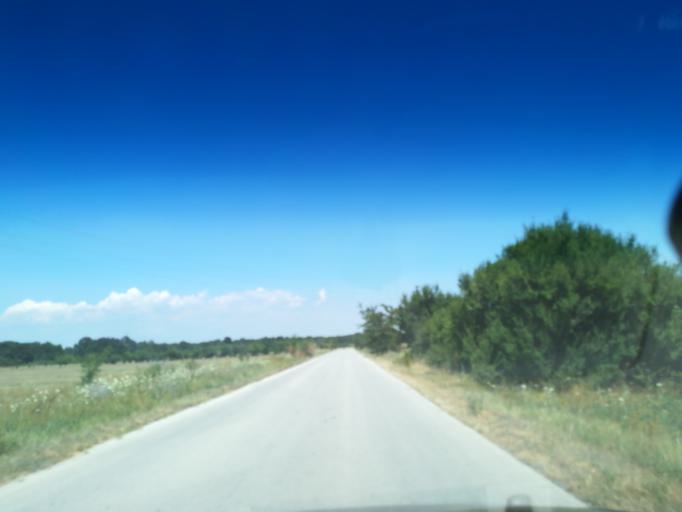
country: BG
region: Plovdiv
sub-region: Obshtina Sadovo
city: Sadovo
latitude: 42.0171
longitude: 25.0763
